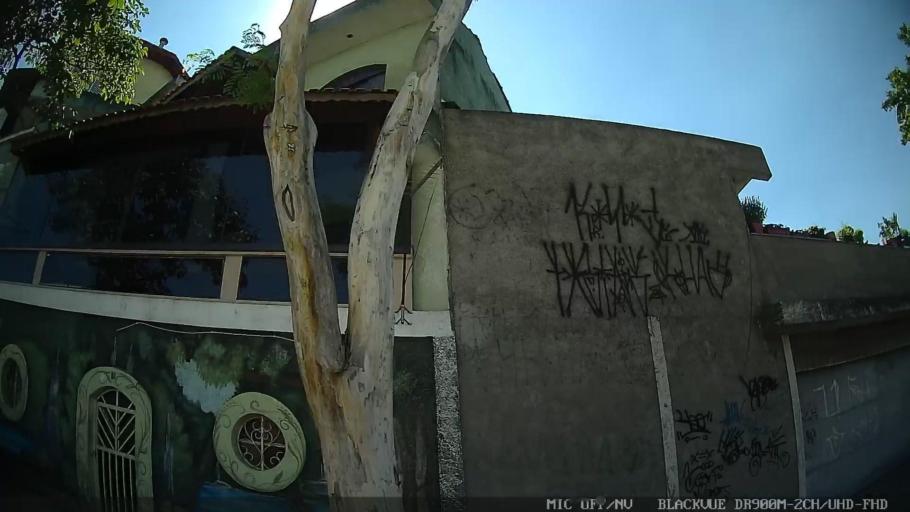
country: BR
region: Sao Paulo
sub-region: Sao Caetano Do Sul
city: Sao Caetano do Sul
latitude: -23.5943
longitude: -46.4984
